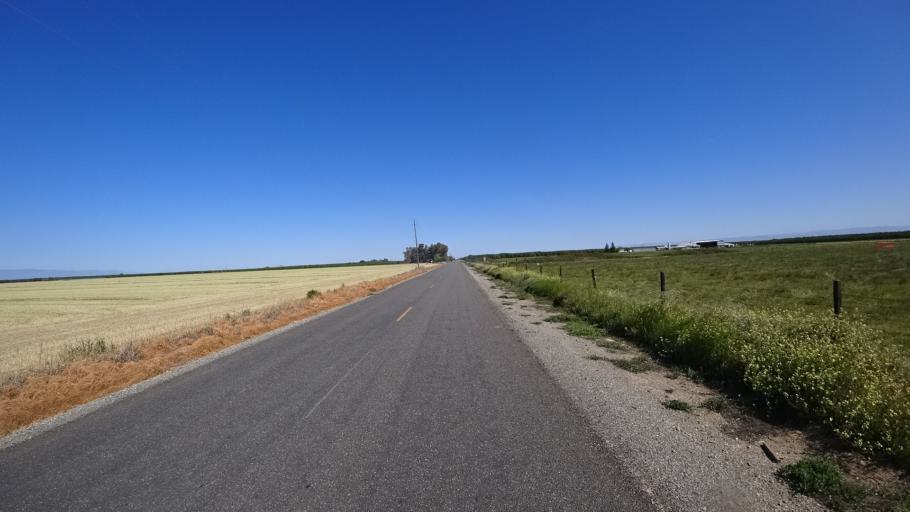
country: US
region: California
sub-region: Glenn County
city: Hamilton City
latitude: 39.6551
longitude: -122.1036
